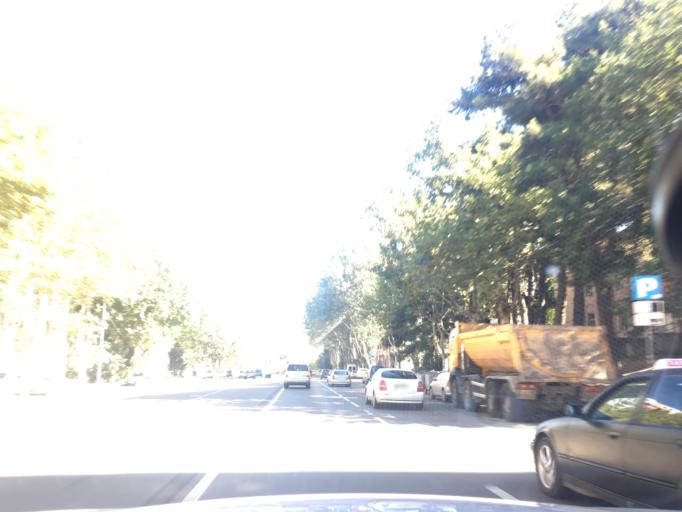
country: GE
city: Zahesi
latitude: 41.7713
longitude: 44.7933
